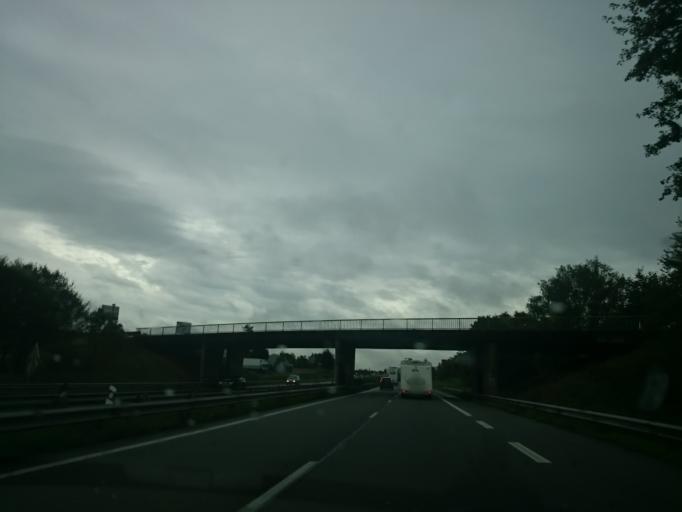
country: FR
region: Pays de la Loire
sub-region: Departement de la Loire-Atlantique
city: Sautron
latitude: 47.2429
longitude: -1.6702
